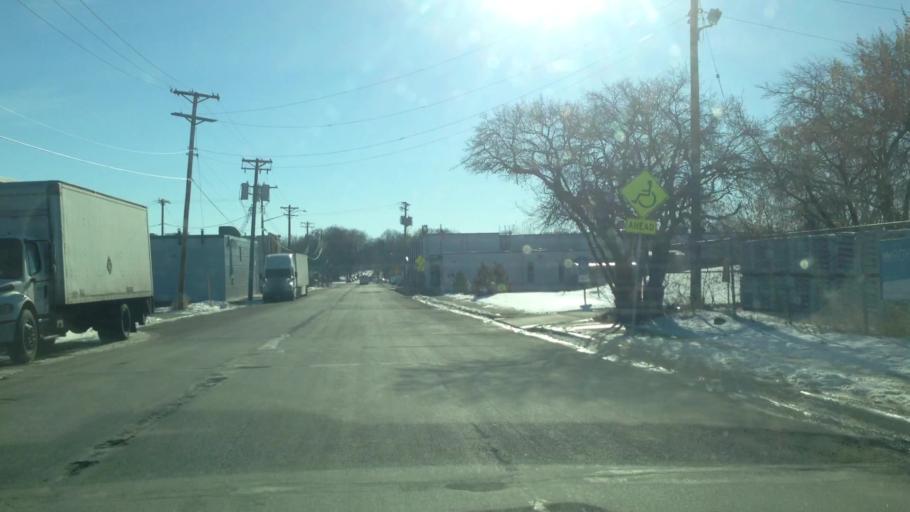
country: US
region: Minnesota
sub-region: Ramsey County
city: Lauderdale
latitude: 44.9944
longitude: -93.2178
